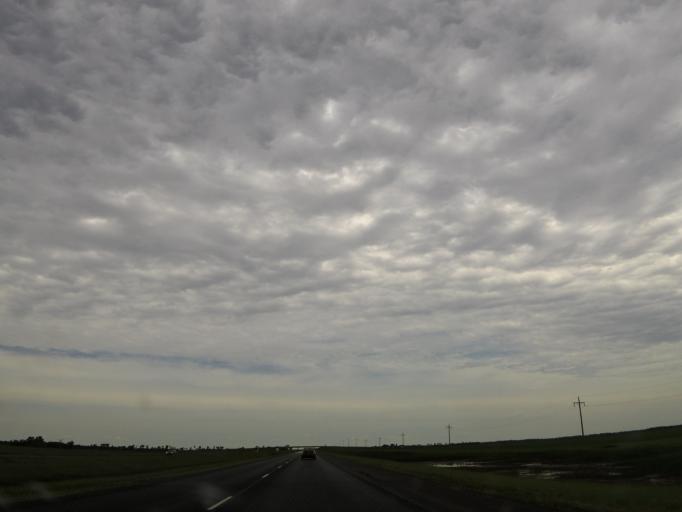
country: US
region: North Dakota
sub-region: Walsh County
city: Grafton
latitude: 48.2577
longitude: -97.1890
